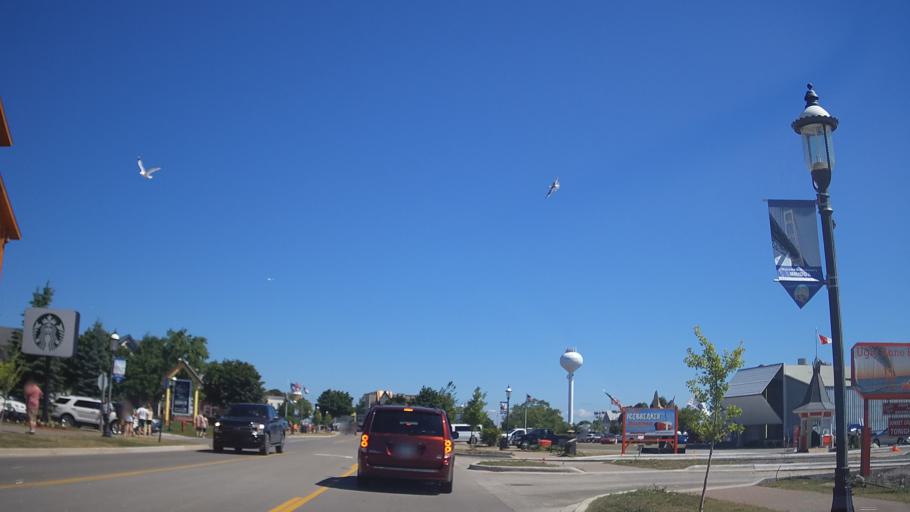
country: US
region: Michigan
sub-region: Mackinac County
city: Saint Ignace
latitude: 45.7795
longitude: -84.7259
